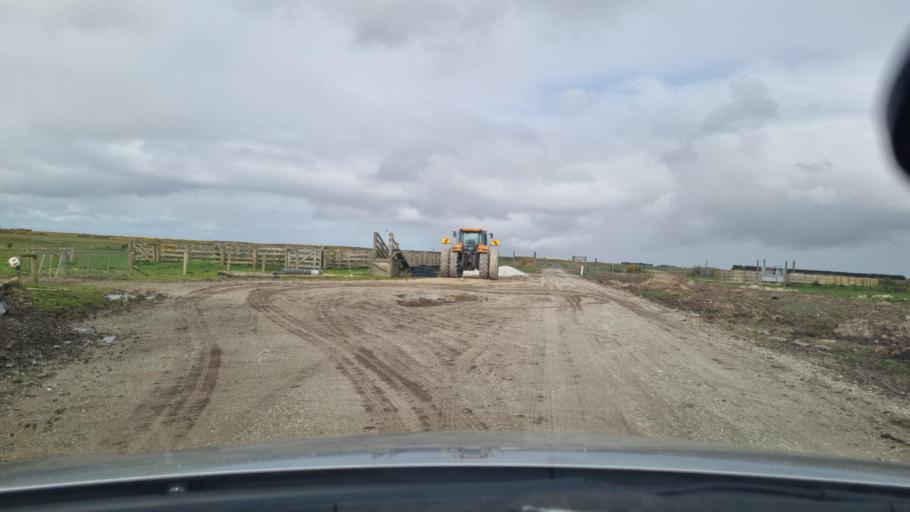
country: NZ
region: Southland
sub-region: Invercargill City
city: Bluff
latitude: -46.5177
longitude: 168.3628
